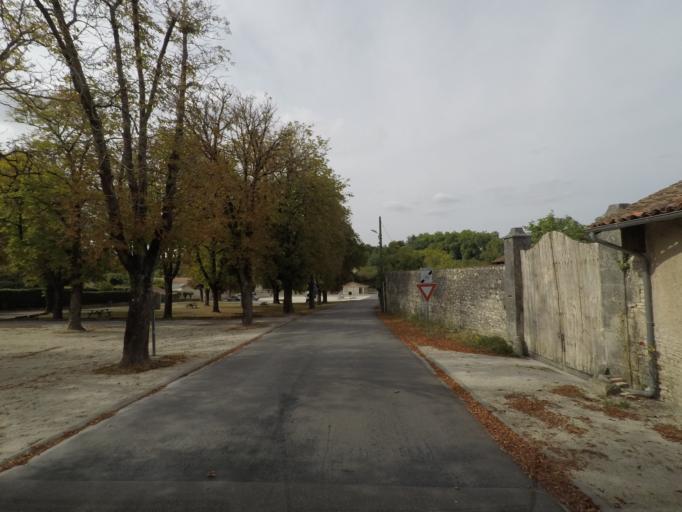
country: FR
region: Poitou-Charentes
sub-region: Departement de la Charente
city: Champagne-Mouton
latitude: 45.9899
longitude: 0.4105
